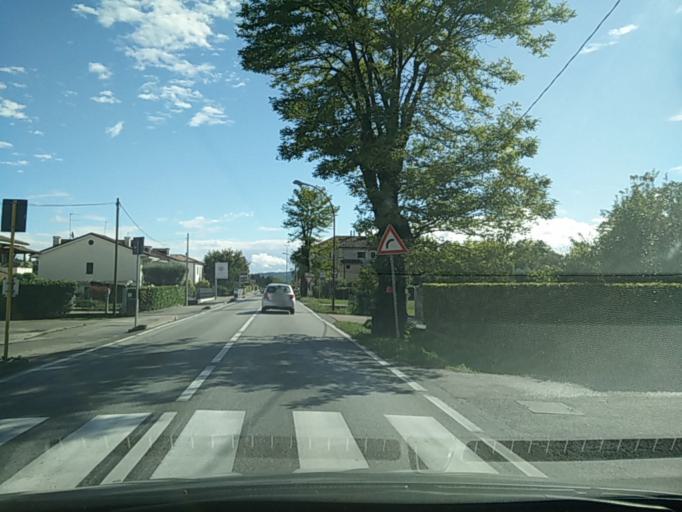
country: IT
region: Veneto
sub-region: Provincia di Treviso
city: Bigolino
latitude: 45.8648
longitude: 12.0203
